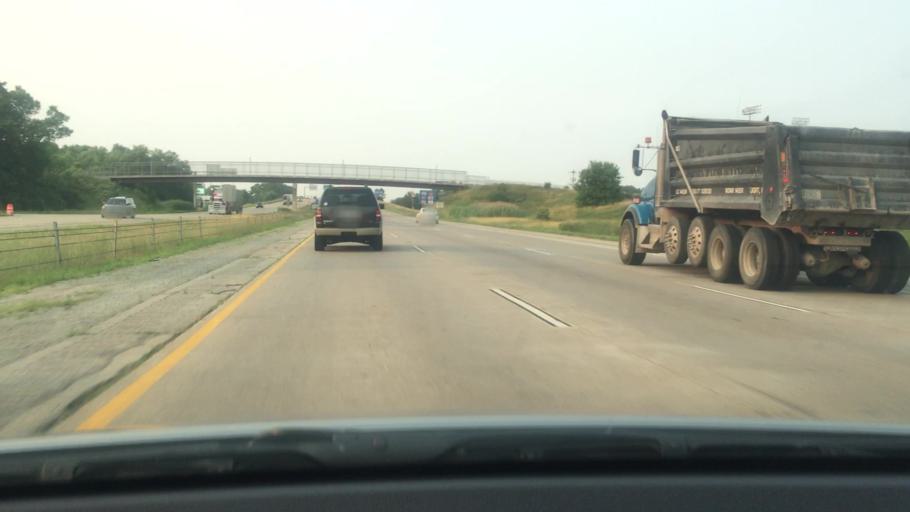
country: US
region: Wisconsin
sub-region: Outagamie County
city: Appleton
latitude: 44.2855
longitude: -88.4664
